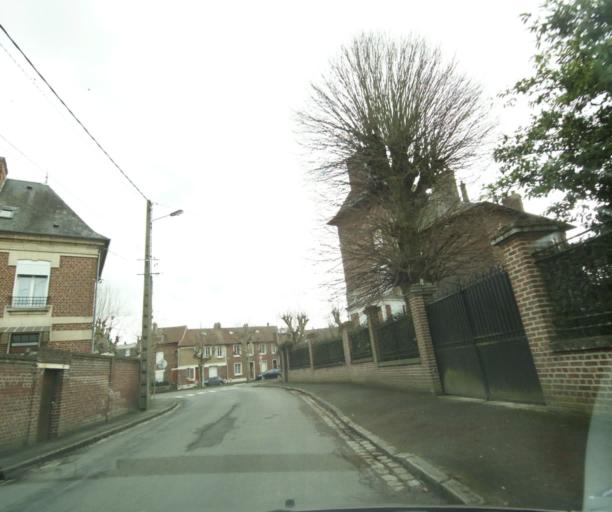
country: FR
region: Picardie
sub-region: Departement de l'Oise
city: Noyon
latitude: 49.5796
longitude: 2.9941
